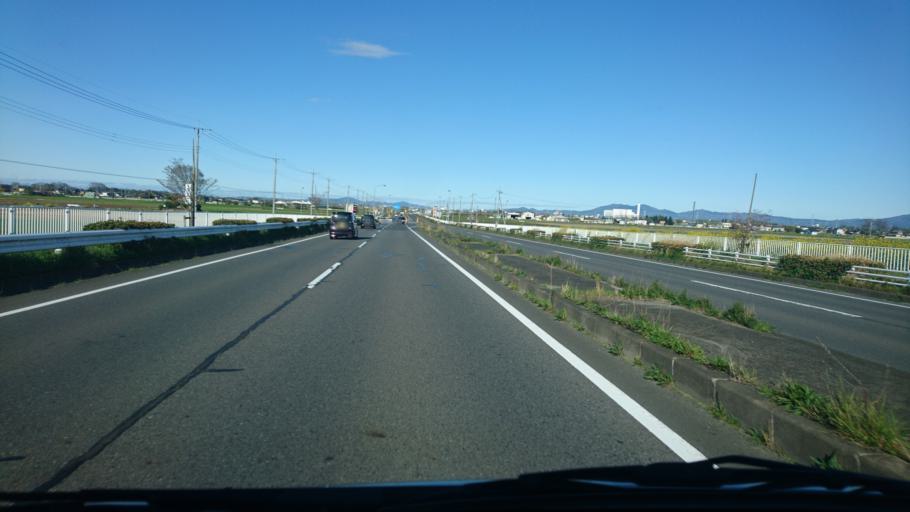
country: JP
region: Ibaraki
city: Yuki
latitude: 36.2889
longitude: 139.8865
